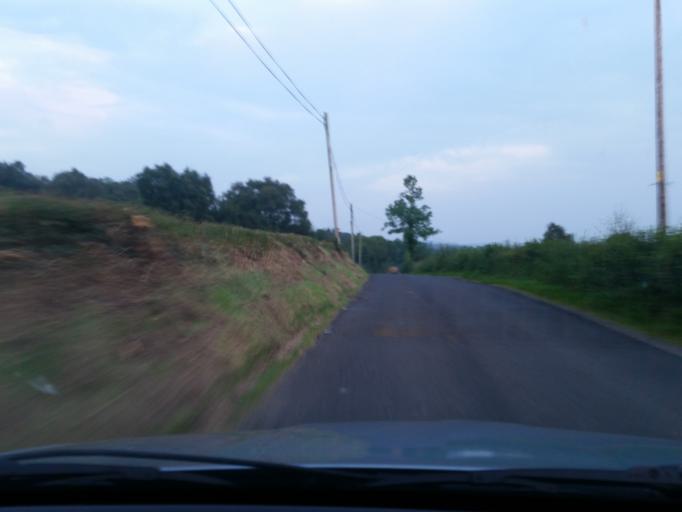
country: GB
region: Northern Ireland
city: Fivemiletown
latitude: 54.3183
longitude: -7.2956
